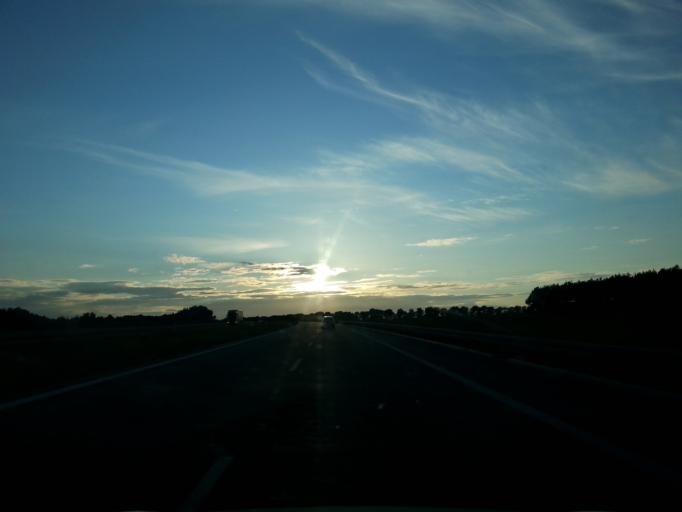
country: PL
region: Lodz Voivodeship
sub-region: Powiat wieruszowski
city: Wieruszow
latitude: 51.3341
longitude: 18.1403
